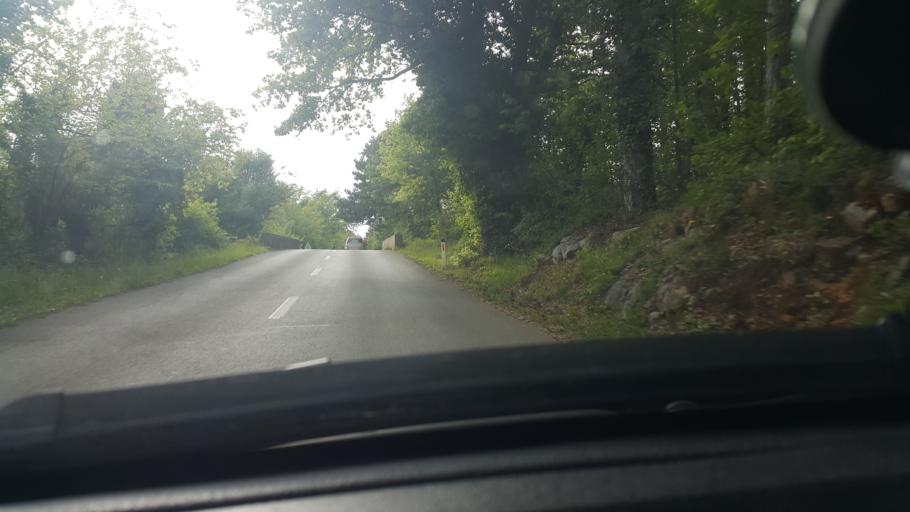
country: IT
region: Friuli Venezia Giulia
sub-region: Provincia di Trieste
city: Zolla
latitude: 45.7586
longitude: 13.8239
